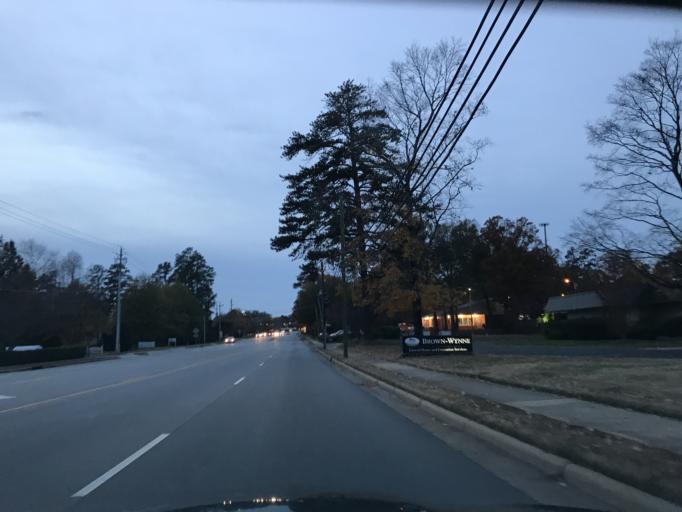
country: US
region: North Carolina
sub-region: Wake County
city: Raleigh
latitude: 35.8502
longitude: -78.6069
